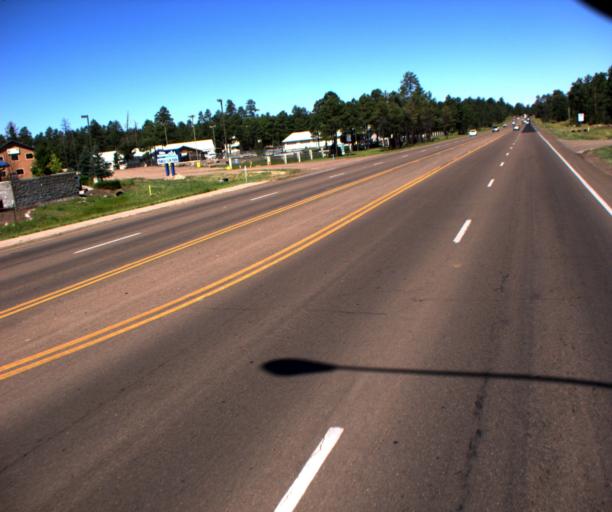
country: US
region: Arizona
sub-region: Navajo County
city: Lake of the Woods
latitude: 34.1730
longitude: -110.0043
